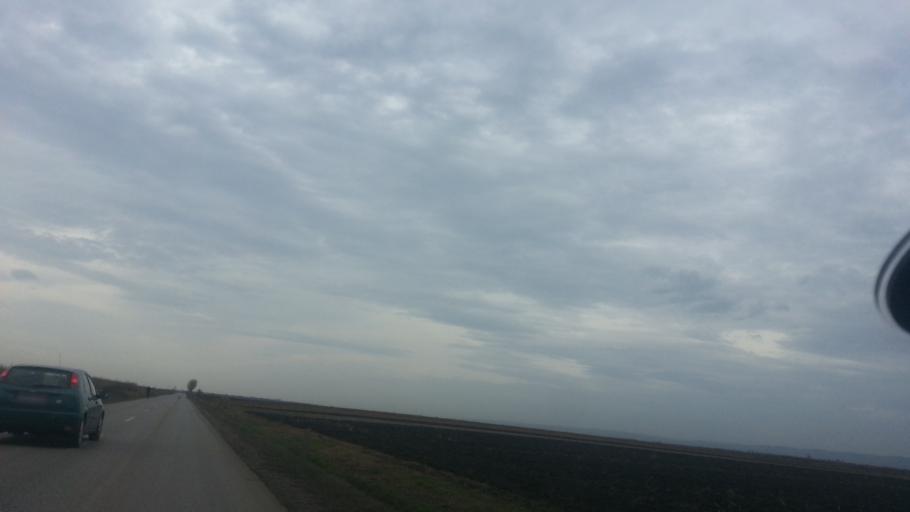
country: RS
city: Golubinci
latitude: 44.9878
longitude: 20.0301
